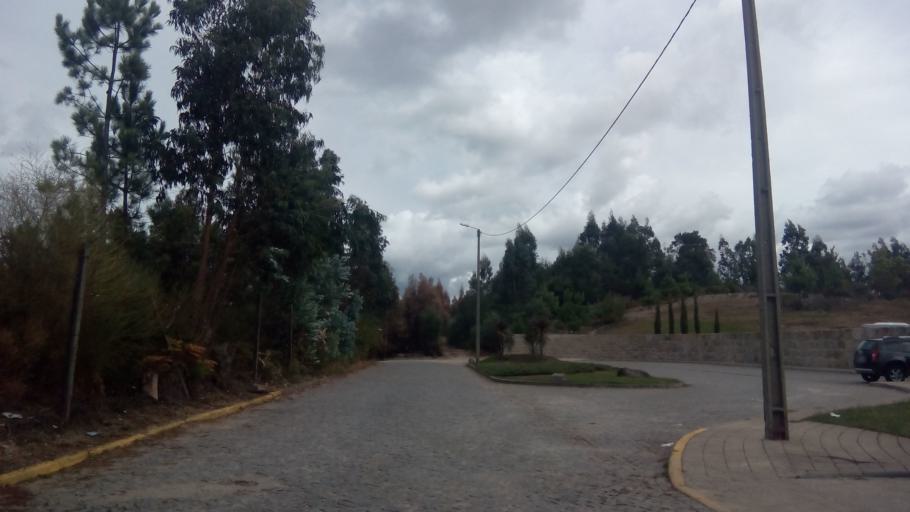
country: PT
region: Porto
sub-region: Paredes
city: Baltar
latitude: 41.1867
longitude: -8.3704
